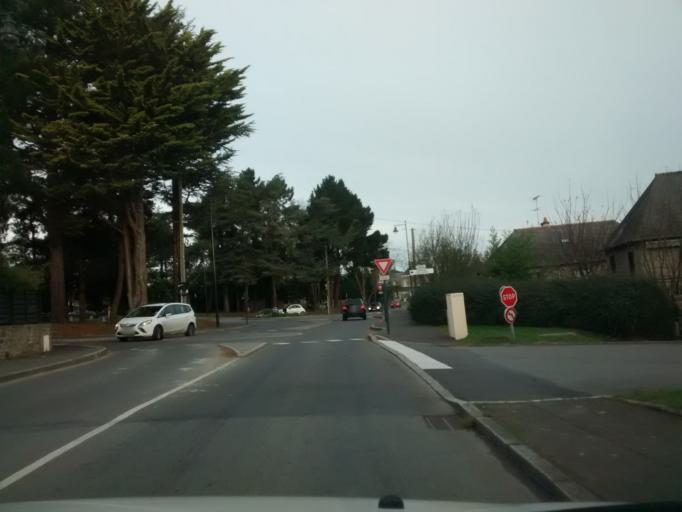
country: FR
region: Brittany
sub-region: Departement d'Ille-et-Vilaine
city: Dinard
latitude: 48.6216
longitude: -2.0586
